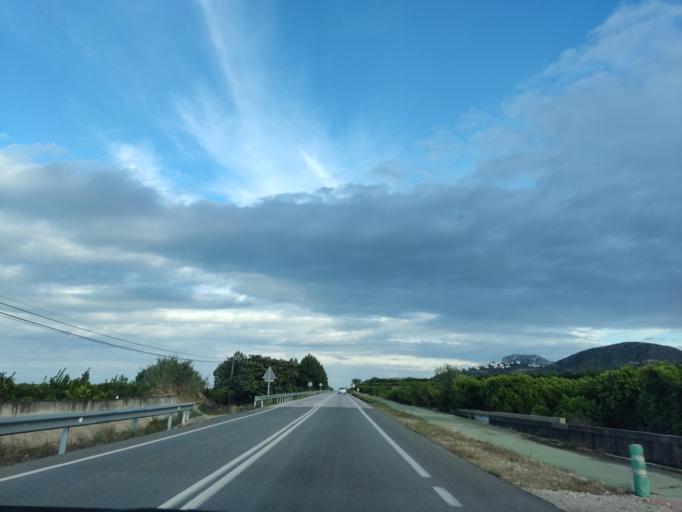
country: ES
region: Valencia
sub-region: Provincia de Alicante
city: Pego
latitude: 38.8459
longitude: -0.0939
